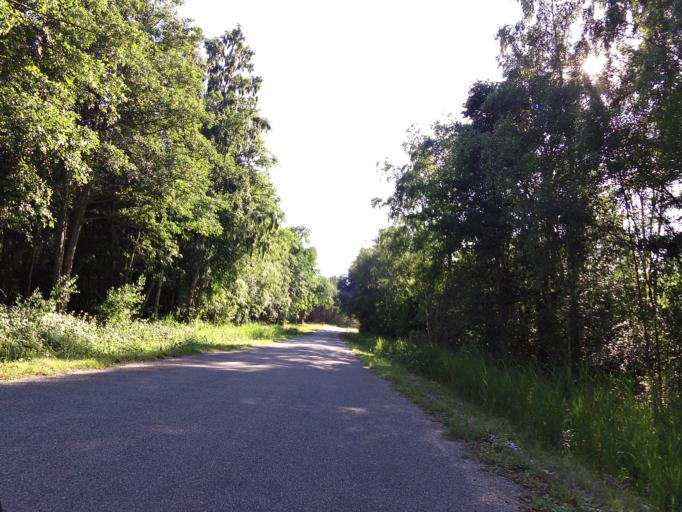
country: EE
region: Hiiumaa
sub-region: Kaerdla linn
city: Kardla
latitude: 58.8896
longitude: 22.2628
